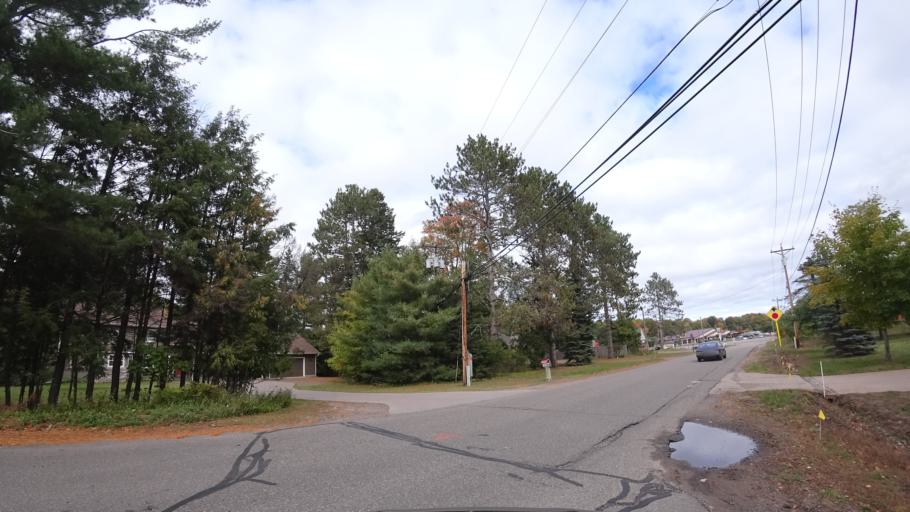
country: US
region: Michigan
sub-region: Marquette County
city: Trowbridge Park
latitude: 46.5477
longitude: -87.4374
